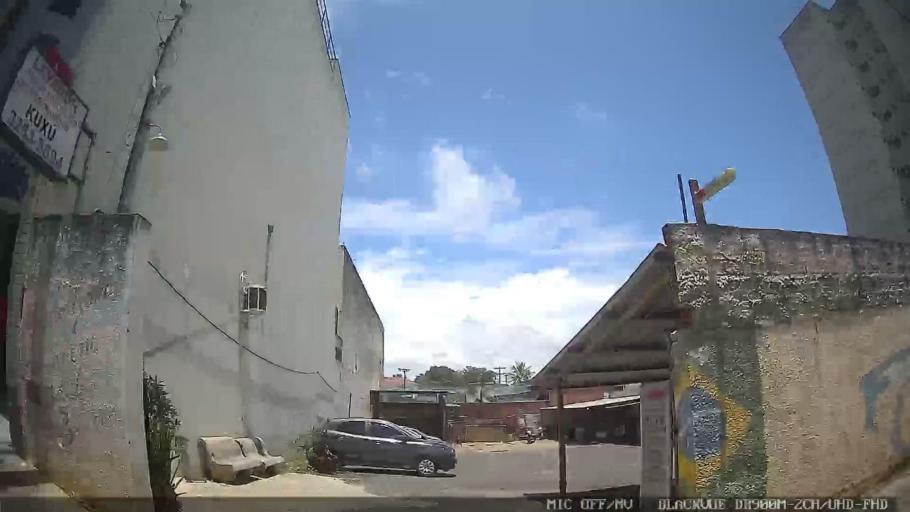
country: BR
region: Sao Paulo
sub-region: Laranjal Paulista
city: Laranjal Paulista
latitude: -23.0514
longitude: -47.8375
